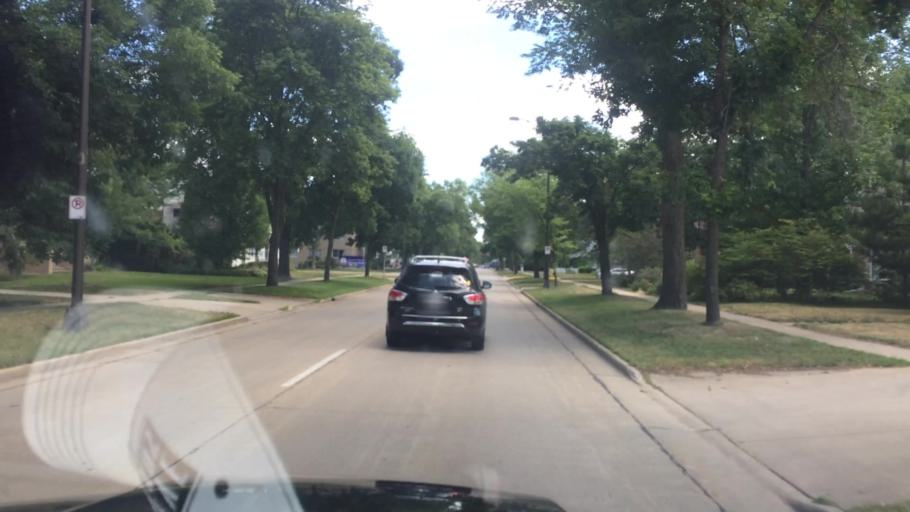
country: US
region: Wisconsin
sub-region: Portage County
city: Stevens Point
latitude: 44.5223
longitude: -89.5693
